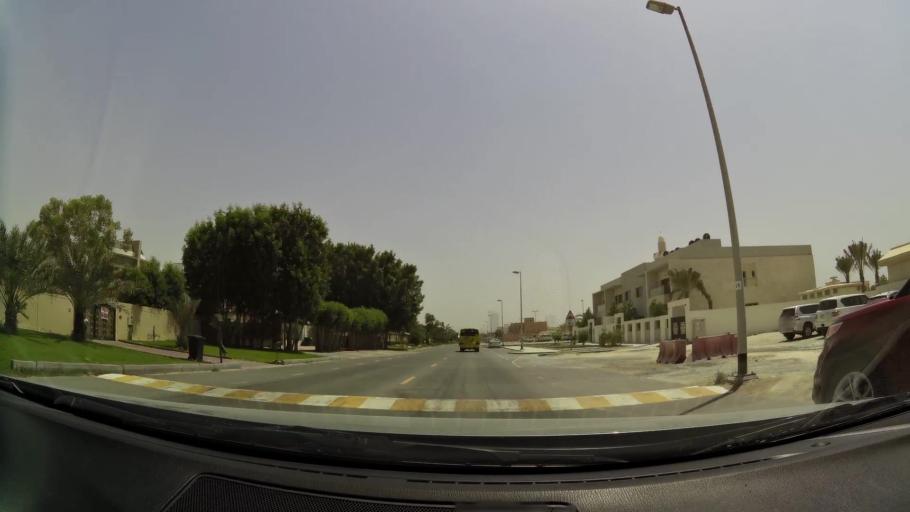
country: AE
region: Dubai
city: Dubai
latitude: 25.1320
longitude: 55.2054
